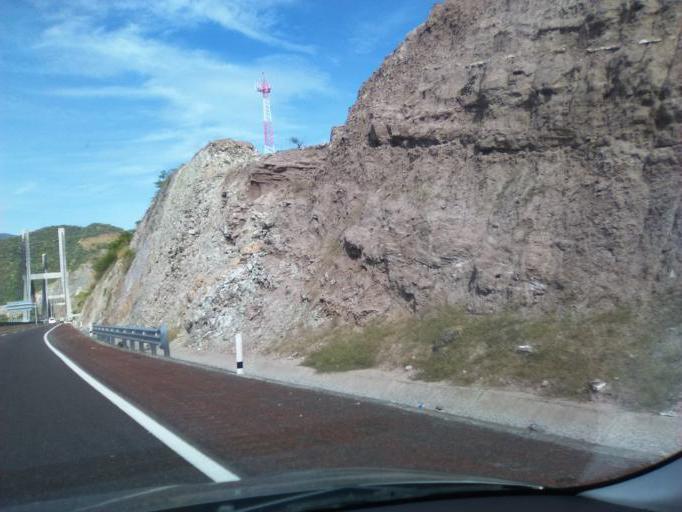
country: MX
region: Guerrero
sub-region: Huitzuco de los Figueroa
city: San Francisco Ozomatlan
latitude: 17.9301
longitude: -99.3735
